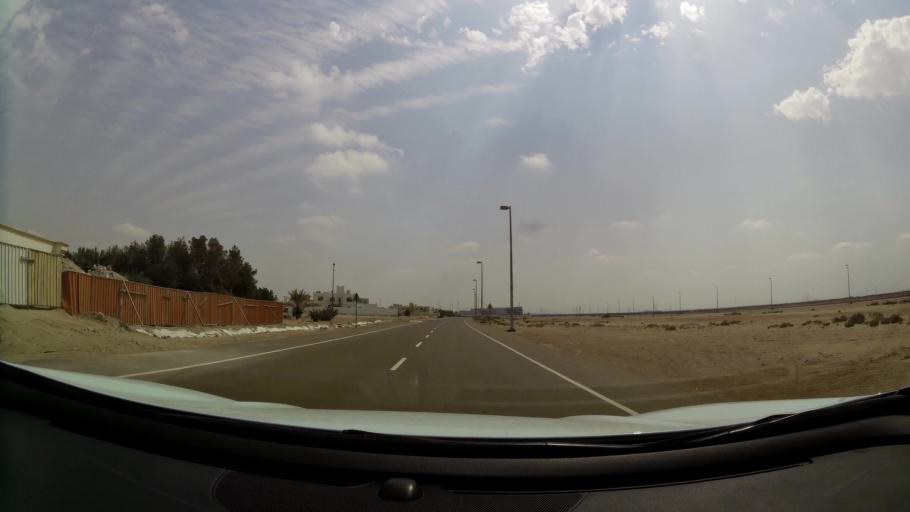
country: AE
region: Abu Dhabi
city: Abu Dhabi
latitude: 24.5427
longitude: 54.6239
